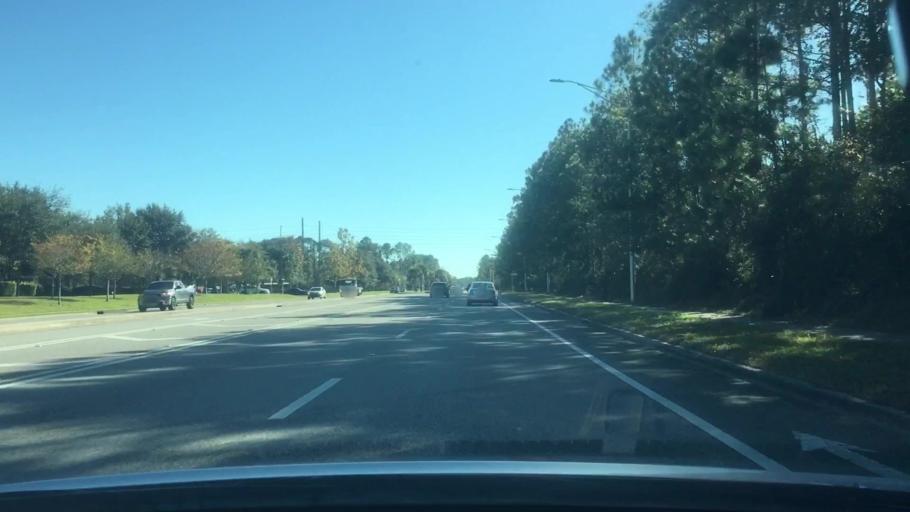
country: US
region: Florida
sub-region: Duval County
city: Neptune Beach
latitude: 30.2991
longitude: -81.4592
